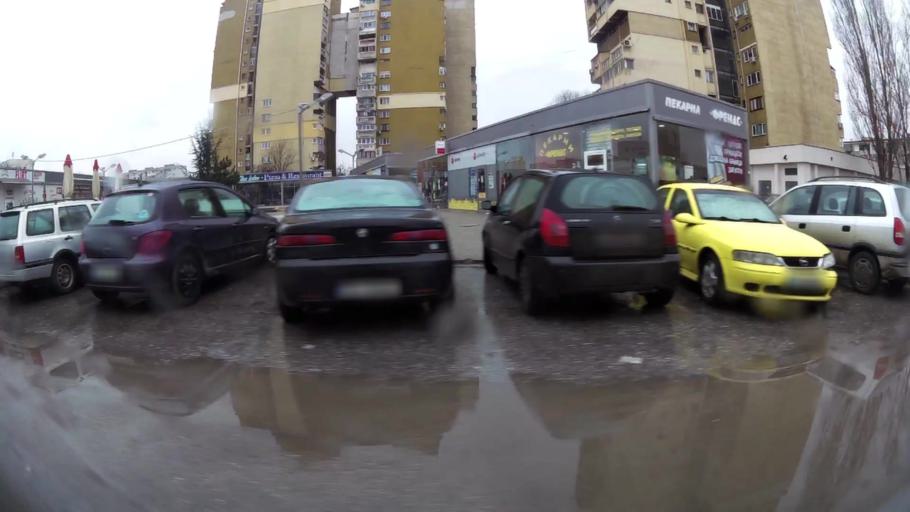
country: BG
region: Sofia-Capital
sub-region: Stolichna Obshtina
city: Sofia
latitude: 42.6619
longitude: 23.3979
